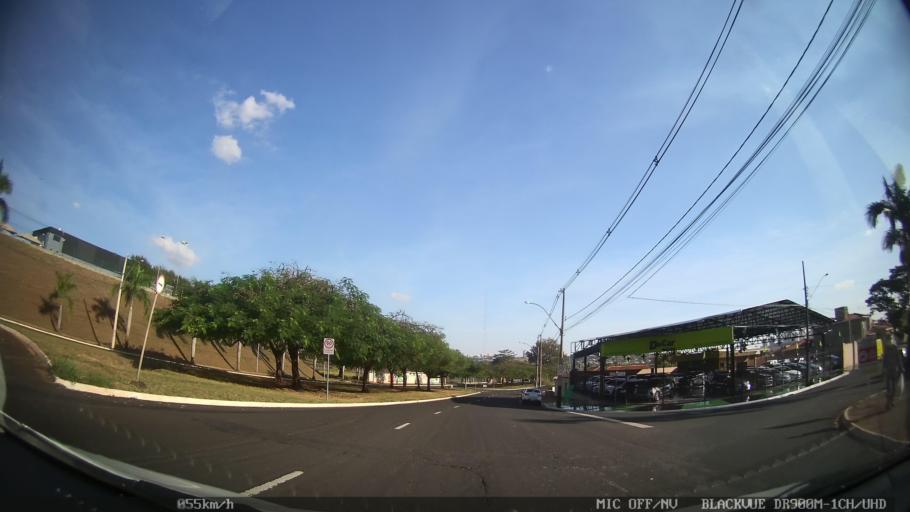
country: BR
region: Sao Paulo
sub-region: Ribeirao Preto
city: Ribeirao Preto
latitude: -21.2088
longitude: -47.7707
